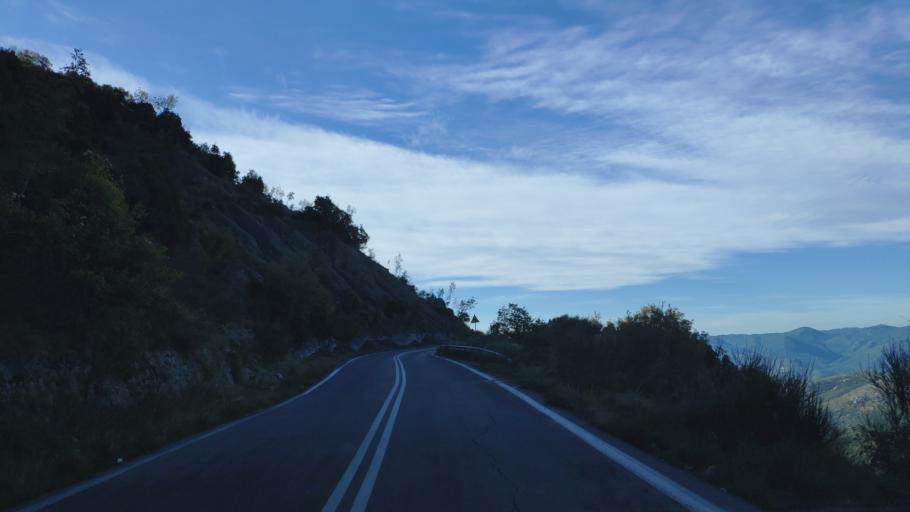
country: GR
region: Peloponnese
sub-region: Nomos Arkadias
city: Dimitsana
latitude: 37.5630
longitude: 22.0629
